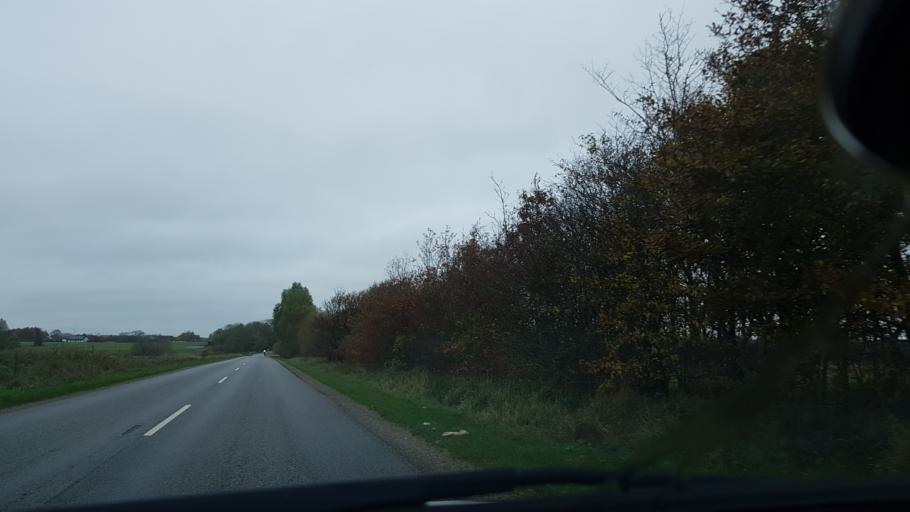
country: DK
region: South Denmark
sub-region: Tonder Kommune
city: Sherrebek
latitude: 55.2402
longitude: 8.8321
